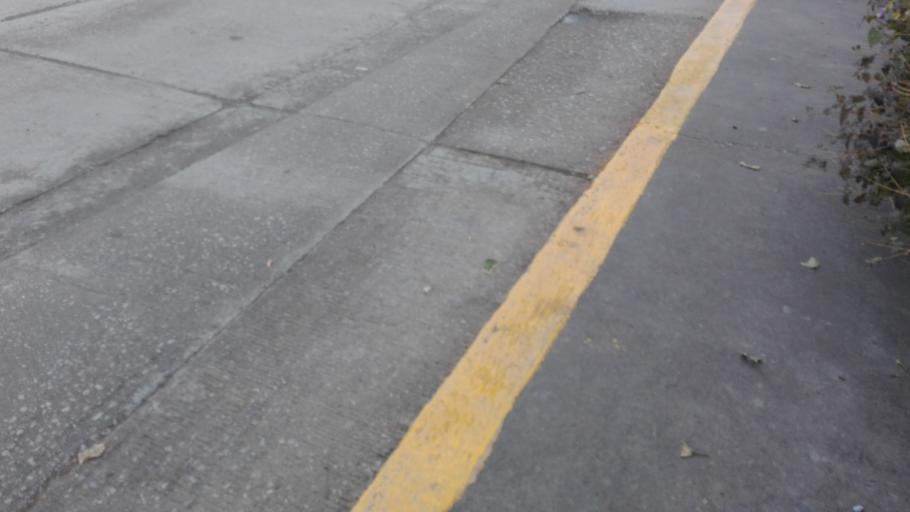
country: MX
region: Chihuahua
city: Ciudad Juarez
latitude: 31.7227
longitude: -106.4194
